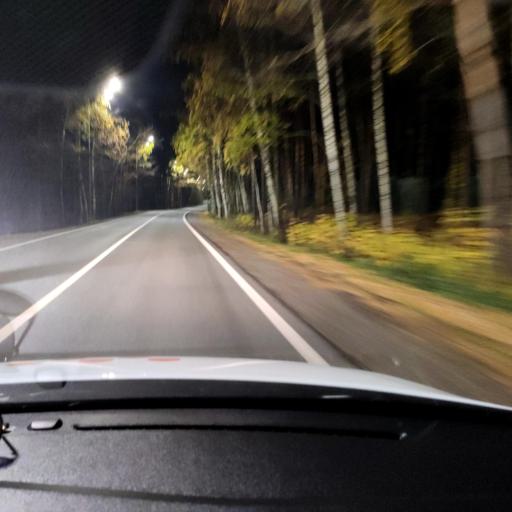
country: RU
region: Tatarstan
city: Verkhniy Uslon
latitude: 55.6317
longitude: 49.0172
